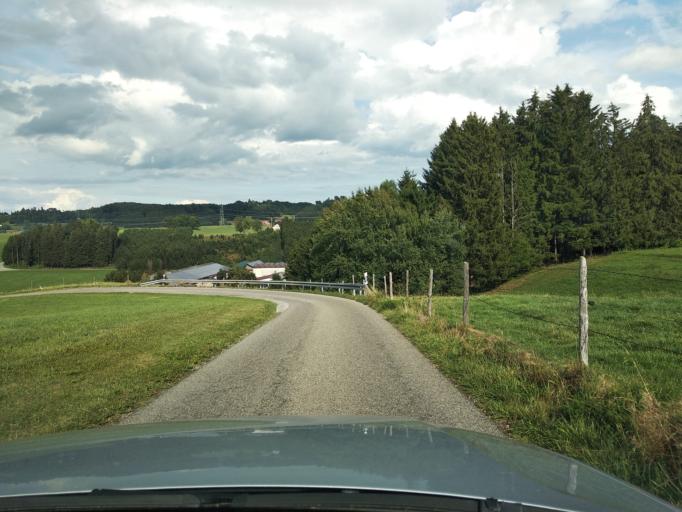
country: DE
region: Bavaria
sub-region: Swabia
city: Wolfertschwenden
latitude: 47.8618
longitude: 10.2518
